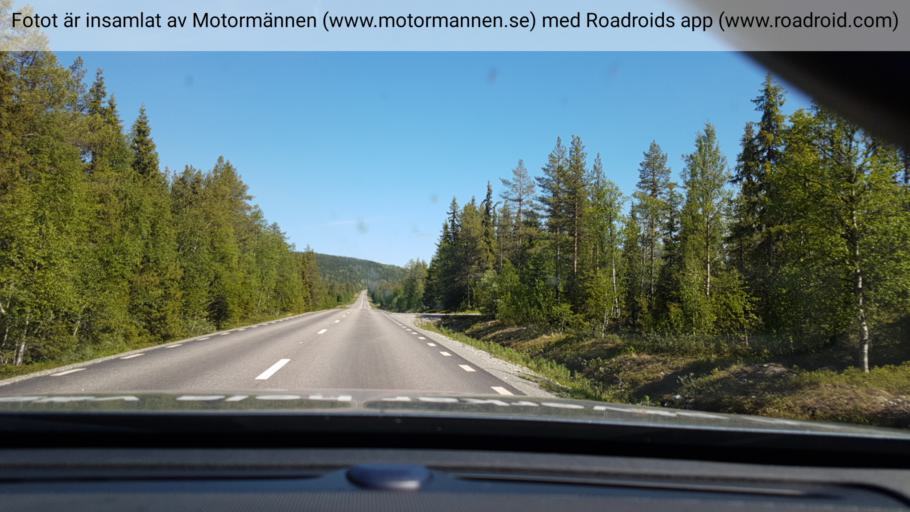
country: SE
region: Vaesterbotten
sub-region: Asele Kommun
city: Insjon
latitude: 64.7225
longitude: 17.6280
